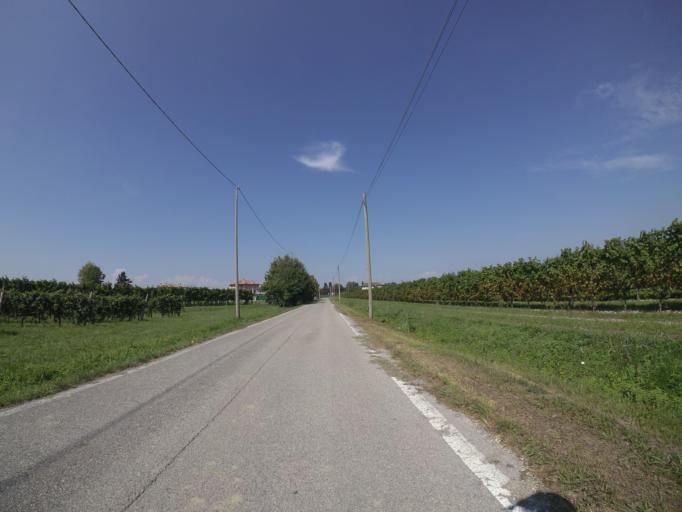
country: IT
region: Friuli Venezia Giulia
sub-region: Provincia di Udine
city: Camino al Tagliamento
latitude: 45.9199
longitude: 12.9426
